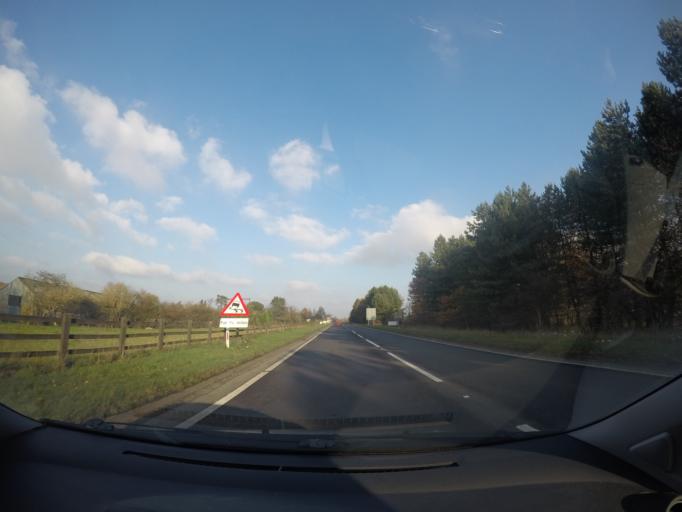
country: GB
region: England
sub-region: City of York
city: Murton
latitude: 53.9996
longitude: -1.0158
